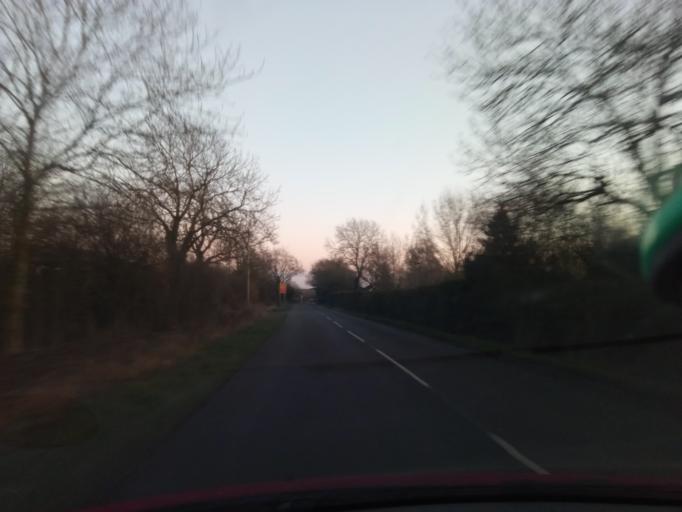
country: GB
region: England
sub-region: Leicestershire
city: Sileby
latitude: 52.7537
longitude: -1.0932
